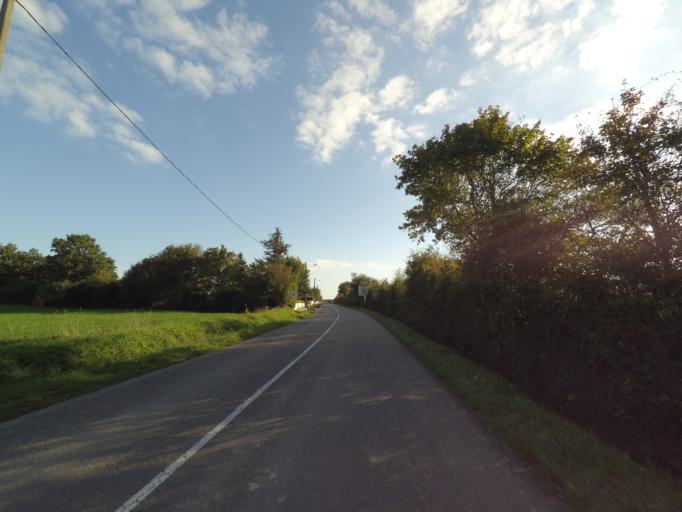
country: FR
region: Pays de la Loire
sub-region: Departement de la Loire-Atlantique
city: Chemere
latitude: 47.1312
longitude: -1.9105
